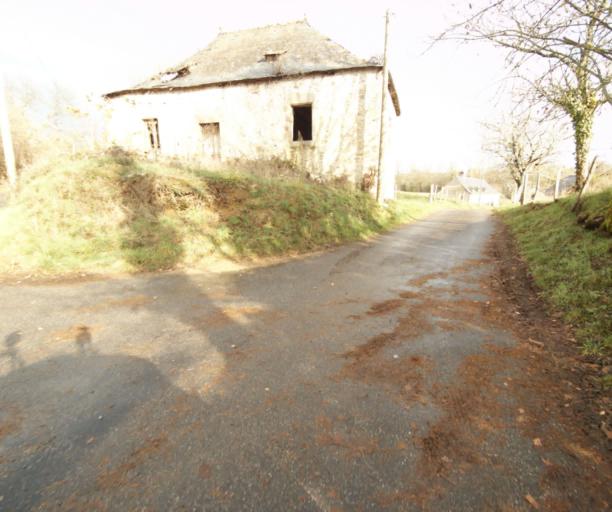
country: FR
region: Limousin
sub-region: Departement de la Correze
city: Saint-Mexant
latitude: 45.2718
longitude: 1.6107
